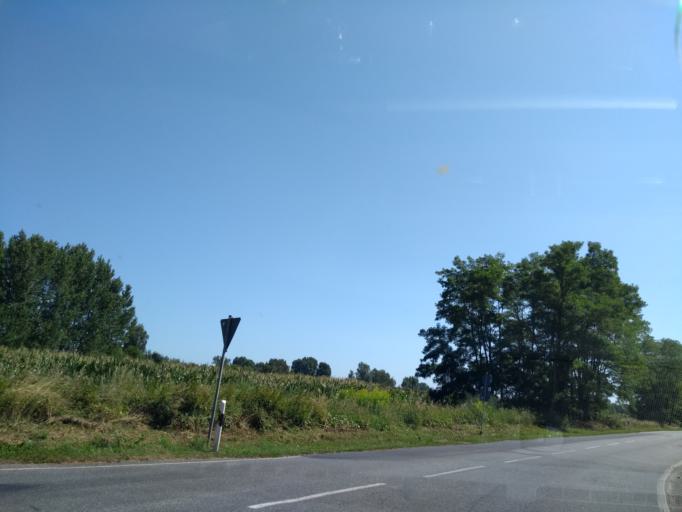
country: DE
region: Brandenburg
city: Lubbenau
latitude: 51.8518
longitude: 13.9495
